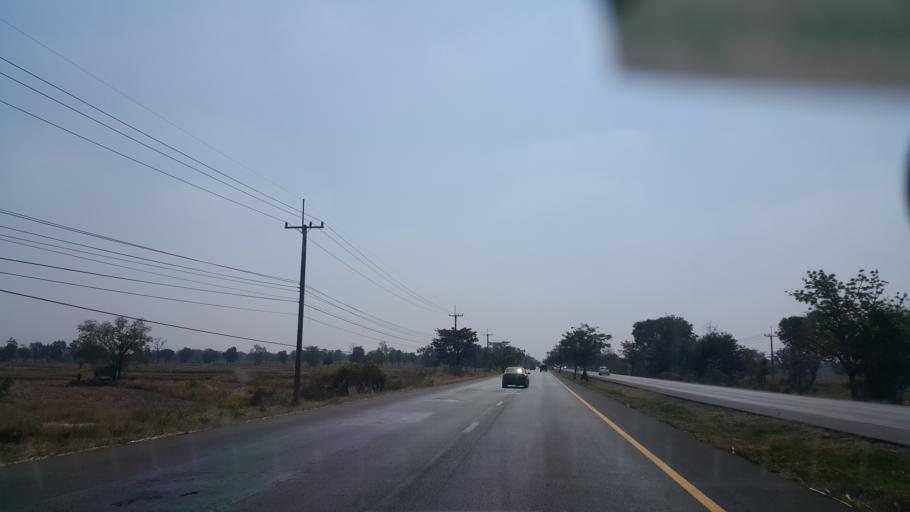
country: TH
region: Nakhon Ratchasima
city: Non Daeng
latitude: 15.3894
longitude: 102.4672
